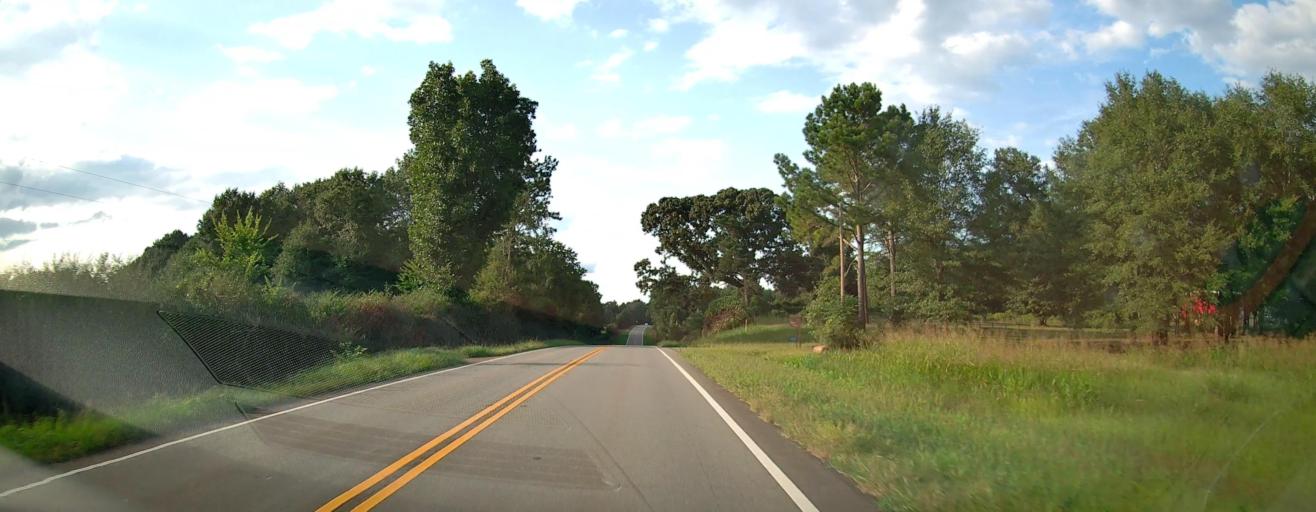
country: US
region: Georgia
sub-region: Monroe County
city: Forsyth
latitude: 32.9566
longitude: -83.9572
